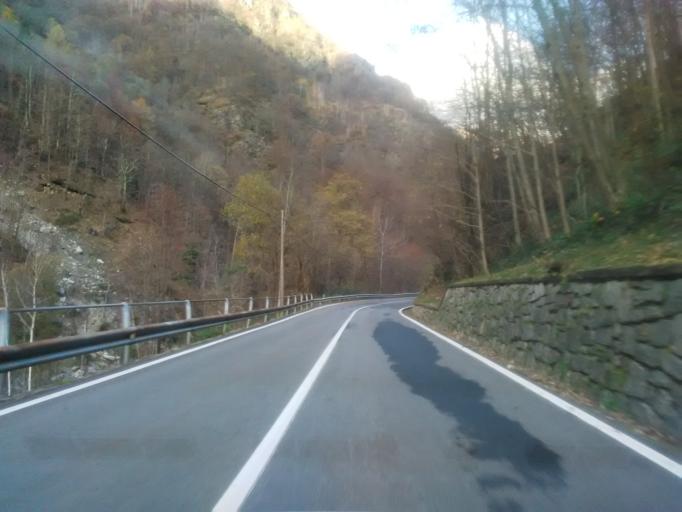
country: IT
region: Piedmont
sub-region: Provincia di Vercelli
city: Cravagliana
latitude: 45.8581
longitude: 8.1846
